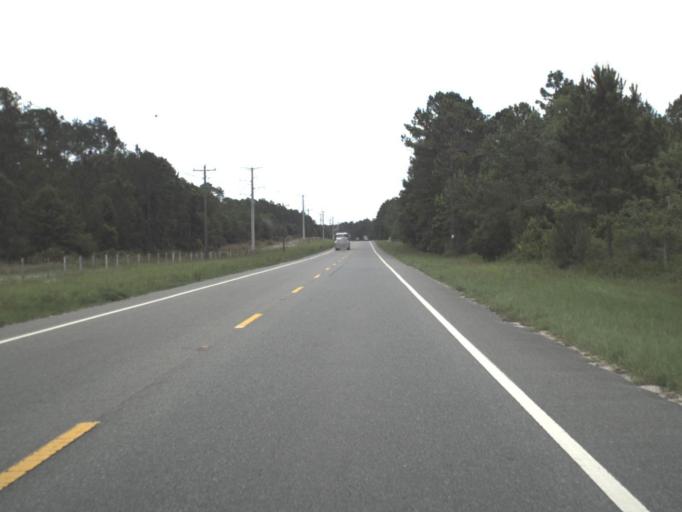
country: US
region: Florida
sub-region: Clay County
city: Keystone Heights
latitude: 29.8907
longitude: -81.9102
